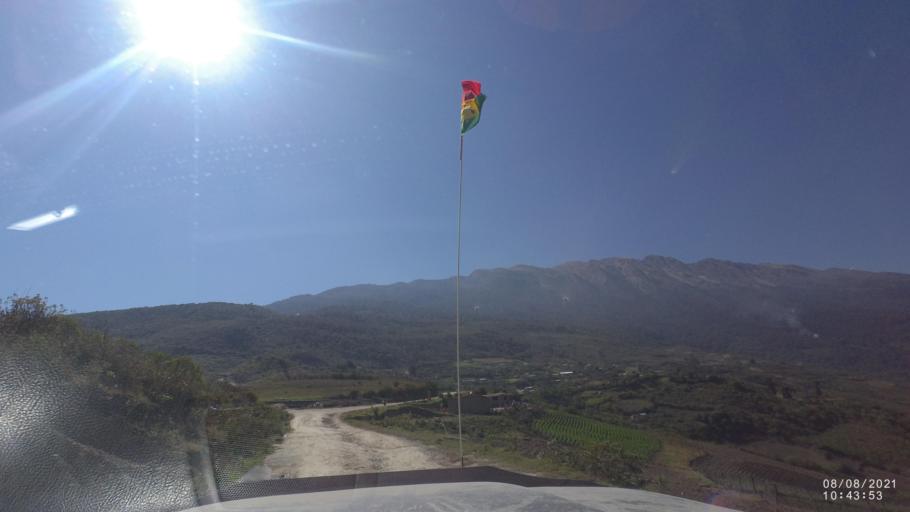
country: BO
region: La Paz
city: Quime
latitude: -16.7041
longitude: -66.7215
